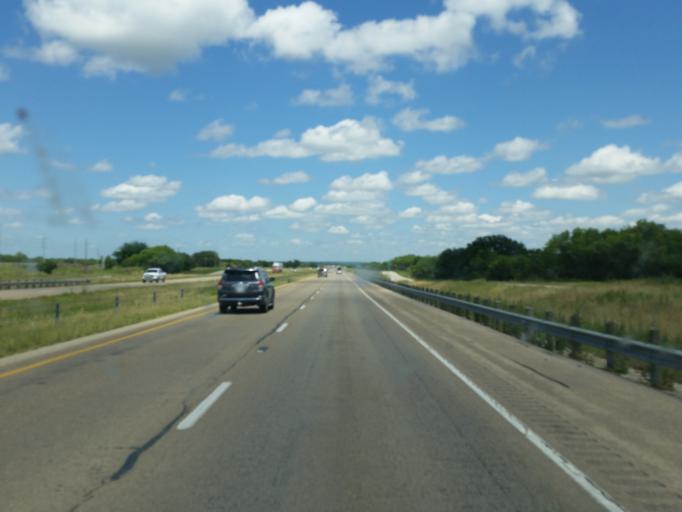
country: US
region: Texas
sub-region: Callahan County
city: Baird
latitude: 32.3902
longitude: -99.3348
